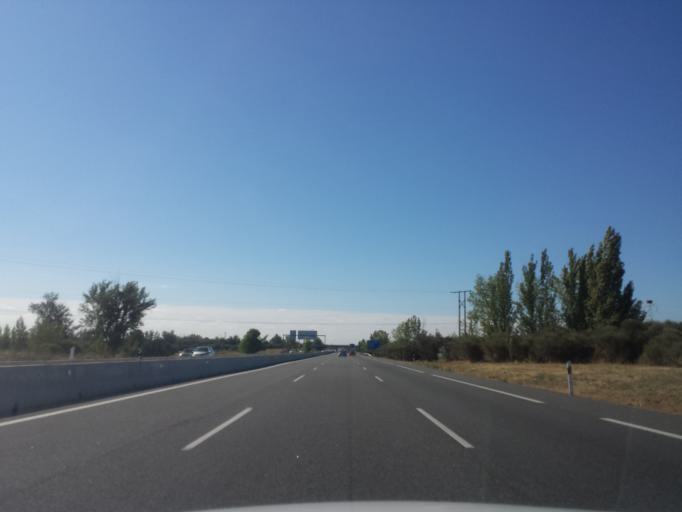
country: ES
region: Castille and Leon
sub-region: Provincia de Zamora
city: Benavente
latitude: 42.0145
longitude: -5.6653
